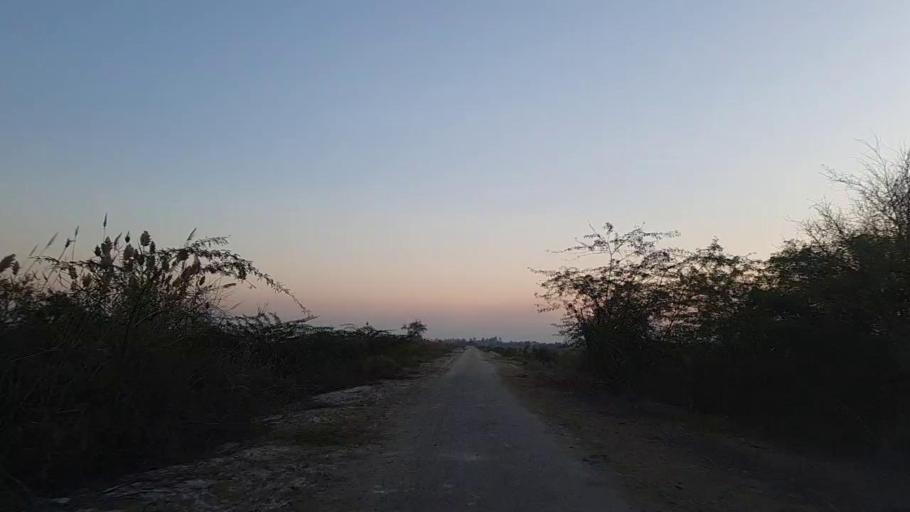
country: PK
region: Sindh
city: Bandhi
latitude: 26.5941
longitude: 68.3360
